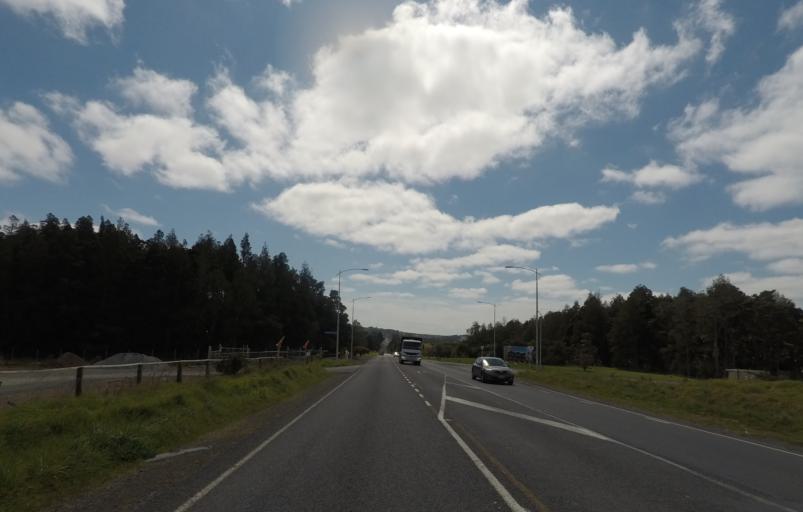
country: NZ
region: Auckland
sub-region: Auckland
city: Manukau City
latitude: -36.9829
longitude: 174.9204
